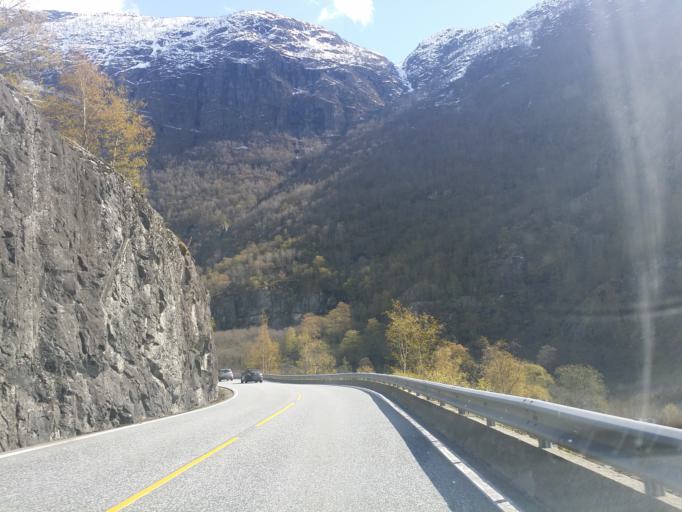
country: NO
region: Hordaland
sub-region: Eidfjord
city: Eidfjord
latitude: 60.4188
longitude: 7.1427
